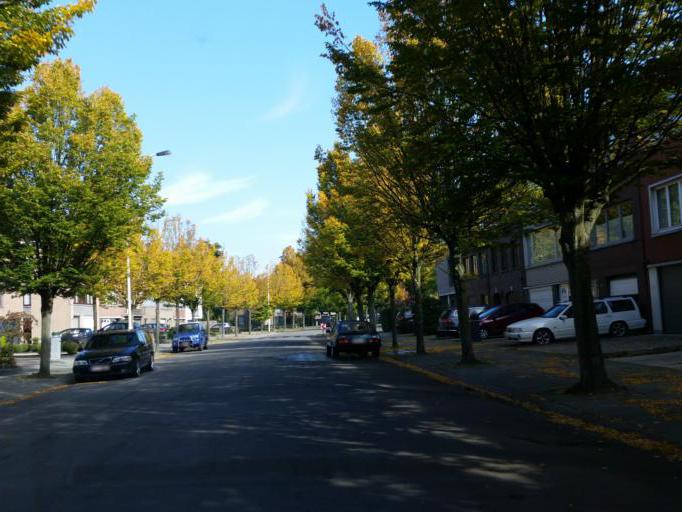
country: BE
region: Flanders
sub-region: Provincie Antwerpen
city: Aartselaar
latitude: 51.1547
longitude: 4.3872
